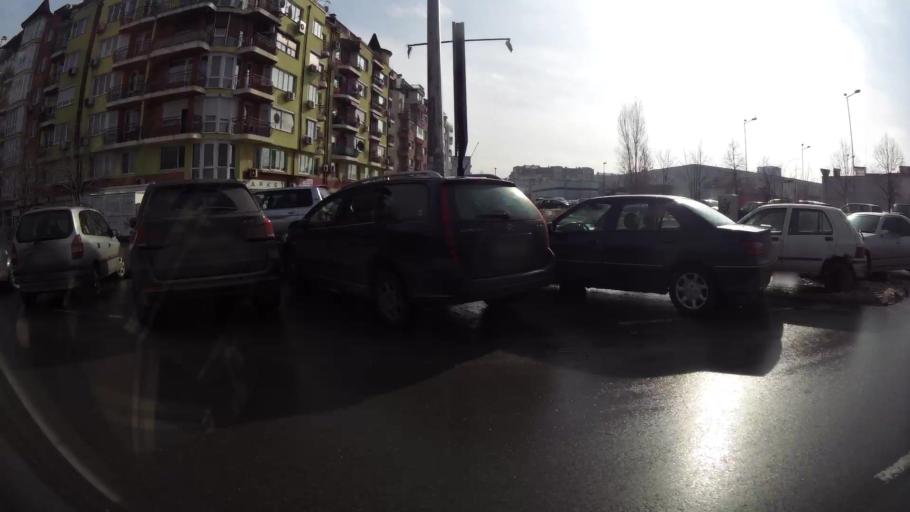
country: BG
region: Sofiya
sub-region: Obshtina Bozhurishte
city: Bozhurishte
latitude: 42.7211
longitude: 23.2561
